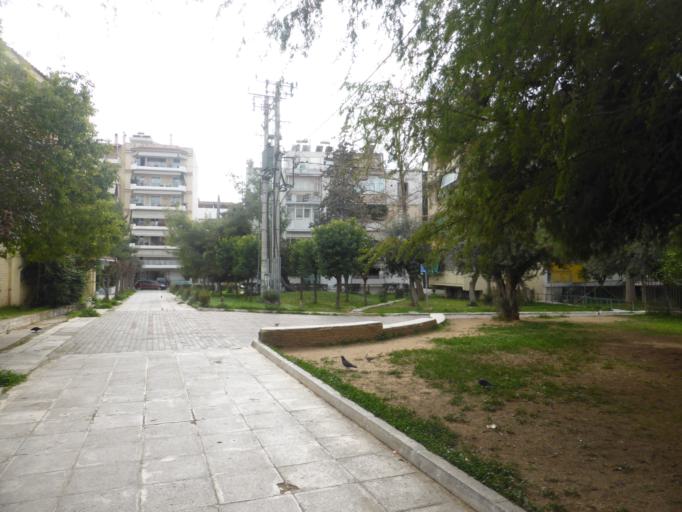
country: GR
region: Attica
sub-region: Nomarchia Athinas
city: Tavros
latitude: 37.9646
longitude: 23.7024
